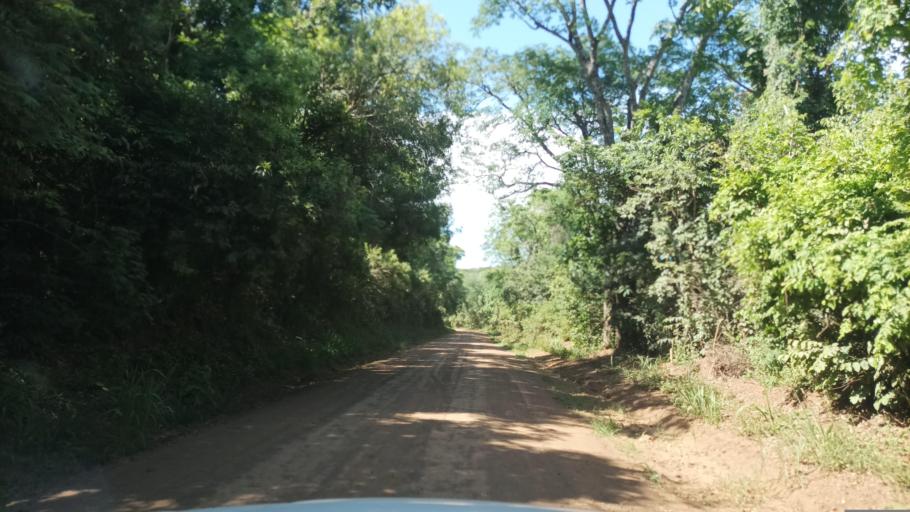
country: AR
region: Misiones
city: Cerro Cora
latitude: -27.5155
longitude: -55.5518
